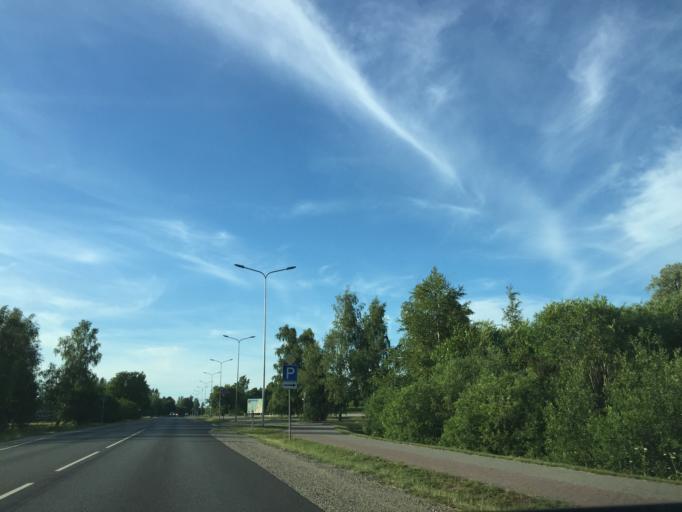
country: LV
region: Ventspils
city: Ventspils
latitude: 57.3579
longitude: 21.5636
